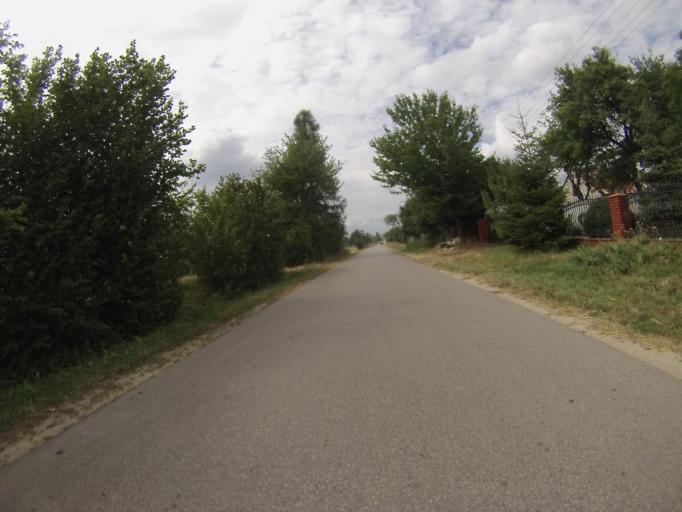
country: PL
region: Swietokrzyskie
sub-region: Powiat kielecki
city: Lagow
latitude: 50.7462
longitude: 21.0871
